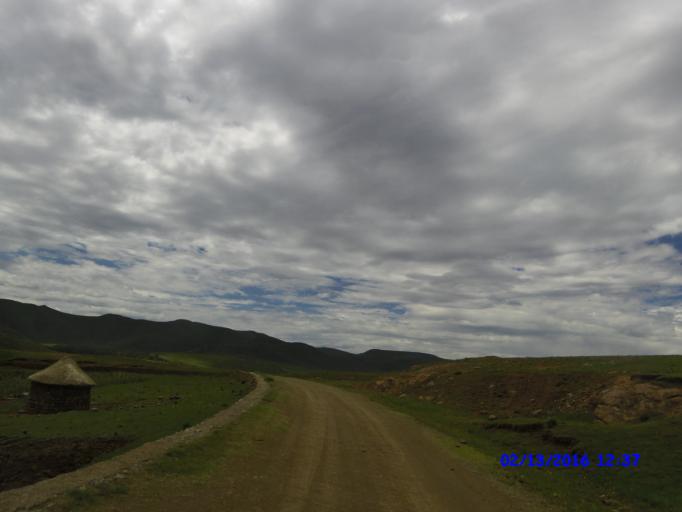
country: LS
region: Maseru
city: Nako
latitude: -29.8374
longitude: 28.0270
